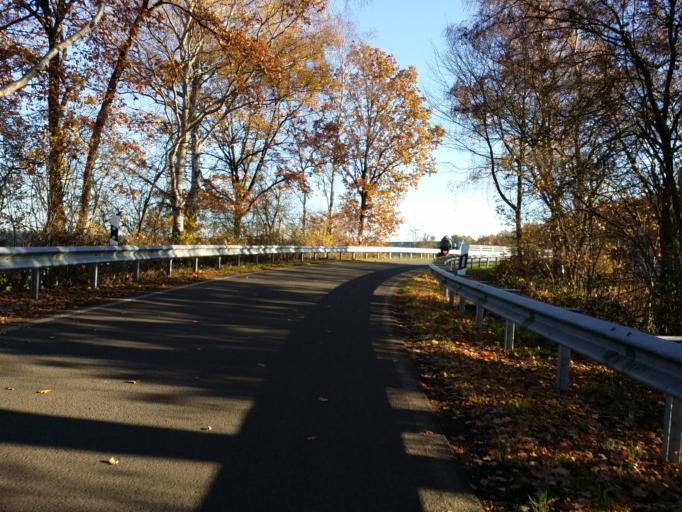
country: DE
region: Lower Saxony
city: Ottersberg
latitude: 53.0616
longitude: 9.0997
